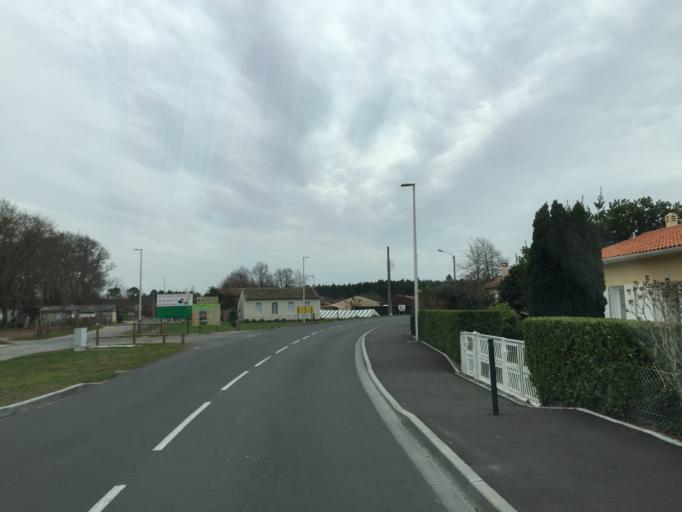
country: FR
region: Aquitaine
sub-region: Departement de la Gironde
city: Carcans
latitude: 45.0746
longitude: -1.0450
